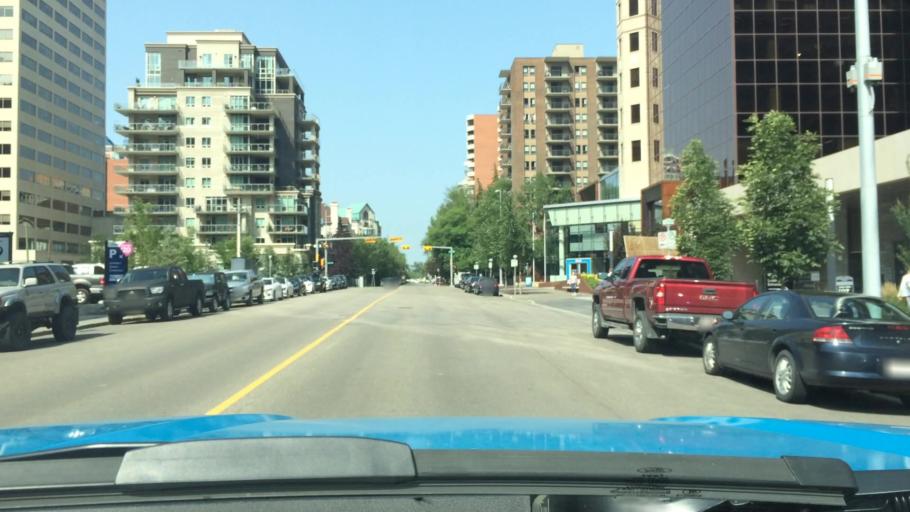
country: CA
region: Alberta
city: Calgary
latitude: 51.0507
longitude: -114.0742
